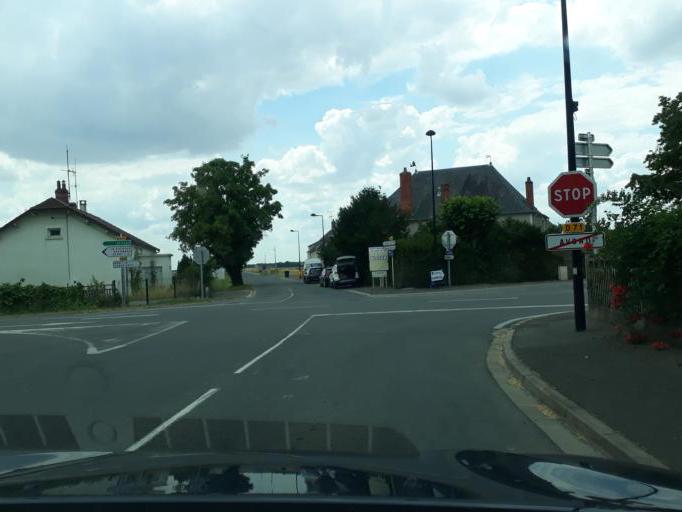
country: FR
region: Centre
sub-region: Departement du Cher
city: Avord
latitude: 47.0309
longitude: 2.6528
